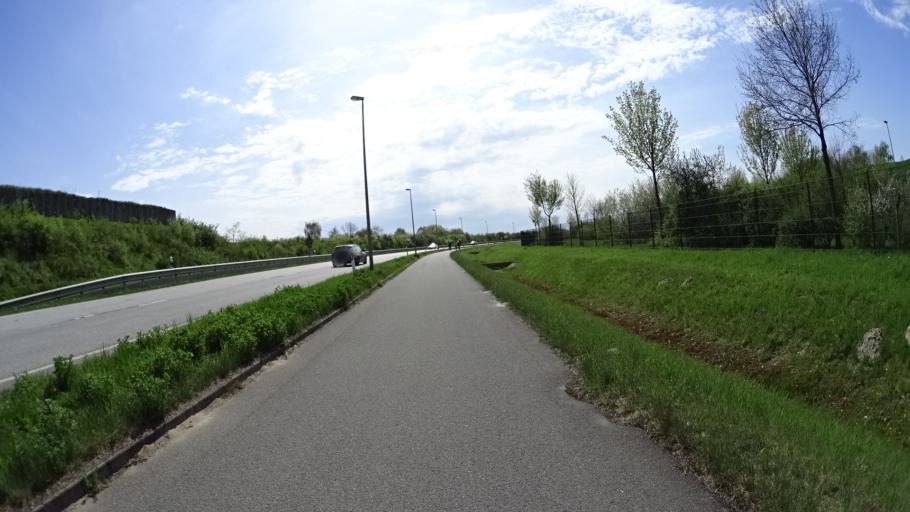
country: DE
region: Lower Saxony
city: Neu Wulmstorf
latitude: 53.5321
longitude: 9.8433
